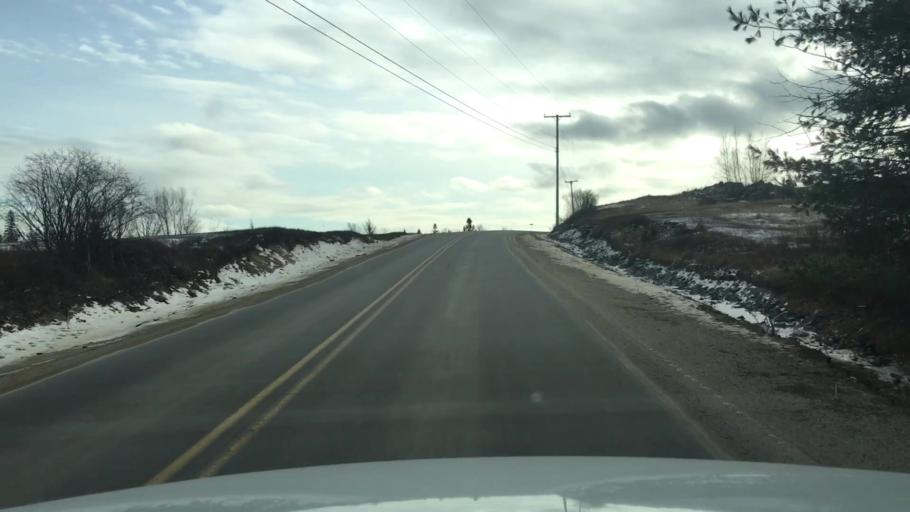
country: US
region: Maine
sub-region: Washington County
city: Jonesport
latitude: 44.6235
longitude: -67.6016
